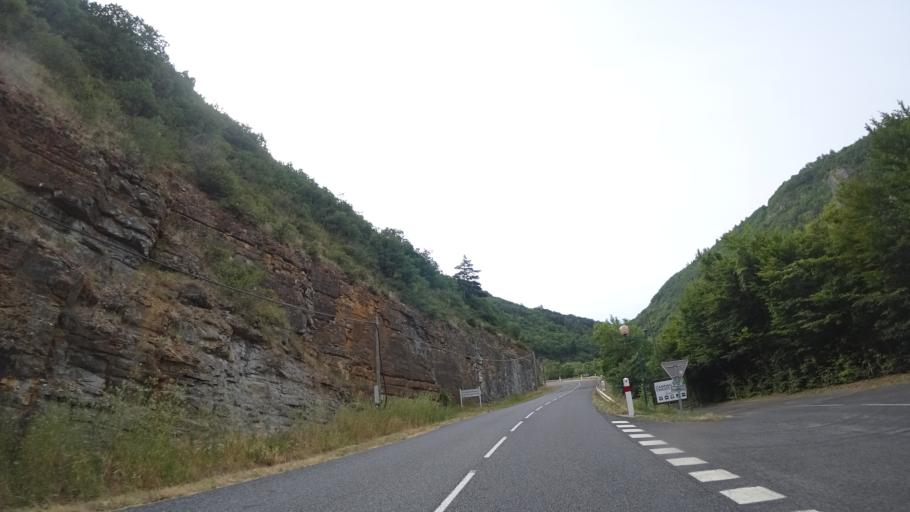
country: FR
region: Languedoc-Roussillon
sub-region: Departement de la Lozere
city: La Canourgue
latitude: 44.4088
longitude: 3.2411
